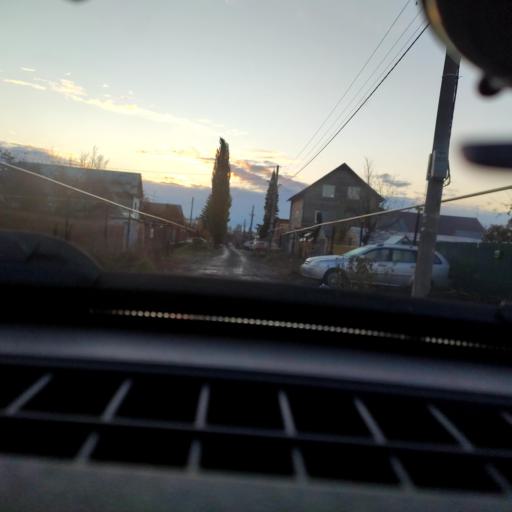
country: RU
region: Bashkortostan
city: Ufa
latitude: 54.8244
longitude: 56.0928
